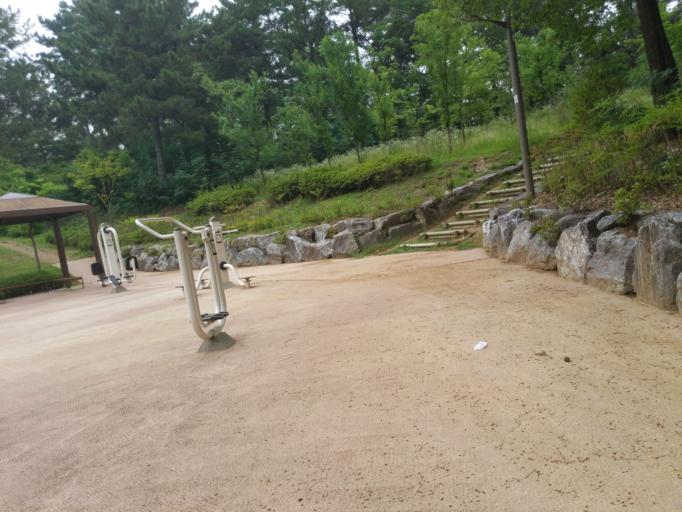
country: KR
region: Daegu
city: Hwawon
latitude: 35.8027
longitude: 128.5333
